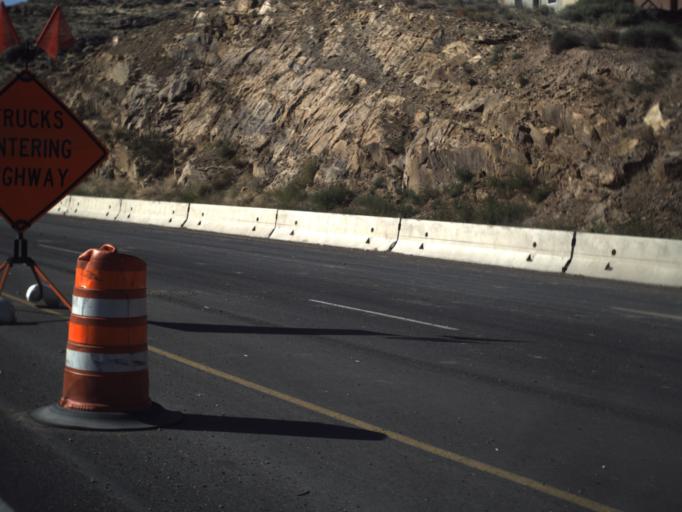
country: US
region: Utah
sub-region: Washington County
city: Saint George
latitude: 37.0726
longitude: -113.5847
